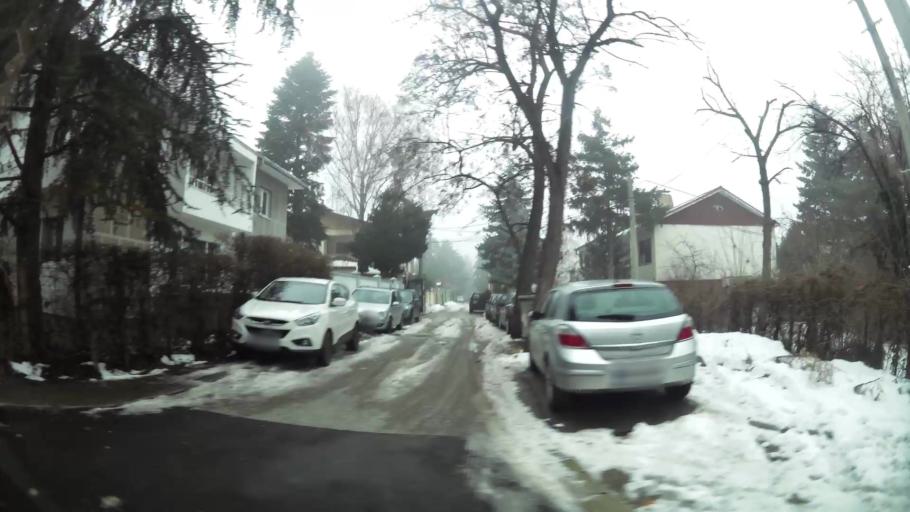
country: RS
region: Central Serbia
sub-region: Belgrade
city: Savski Venac
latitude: 44.7765
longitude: 20.4624
